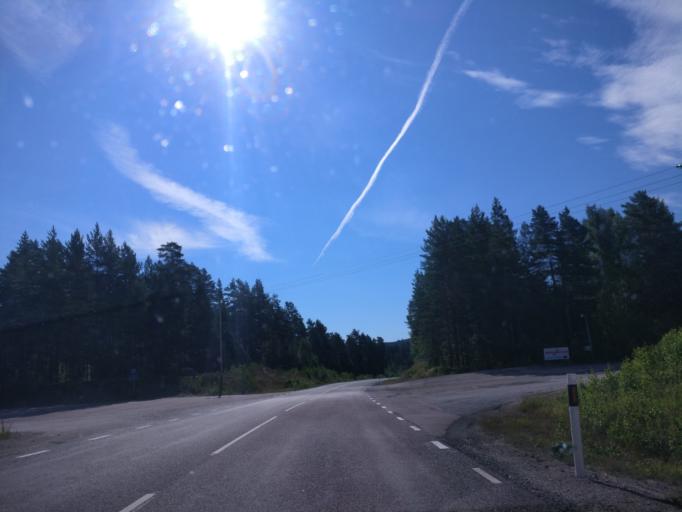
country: SE
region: Vaermland
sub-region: Hagfors Kommun
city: Hagfors
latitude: 60.0634
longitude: 13.7510
